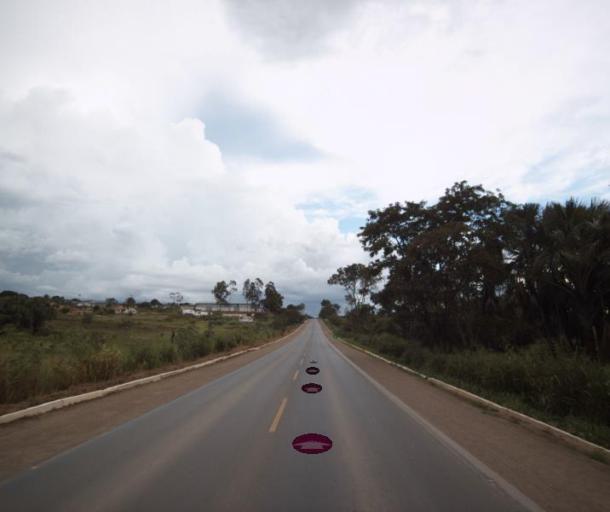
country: BR
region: Goias
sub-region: Itapaci
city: Itapaci
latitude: -14.8688
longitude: -49.3301
